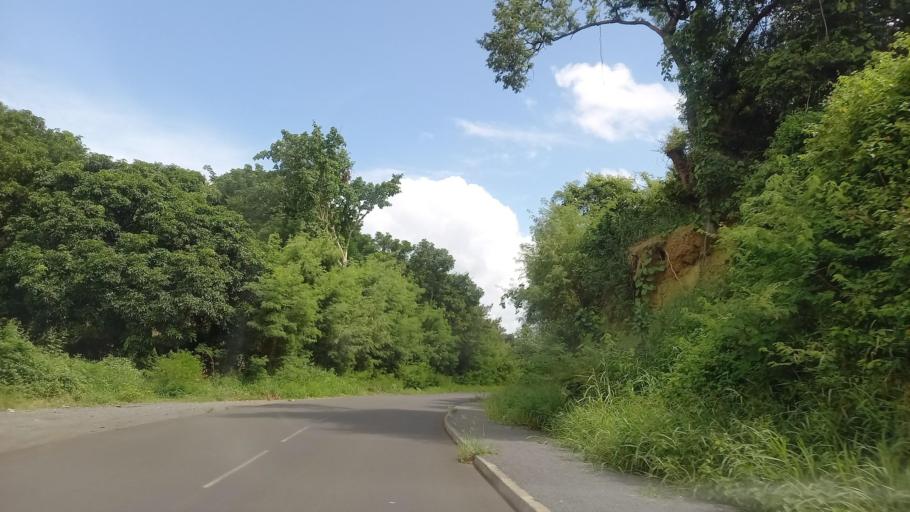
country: YT
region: Boueni
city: Boueni
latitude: -12.9241
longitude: 45.0947
